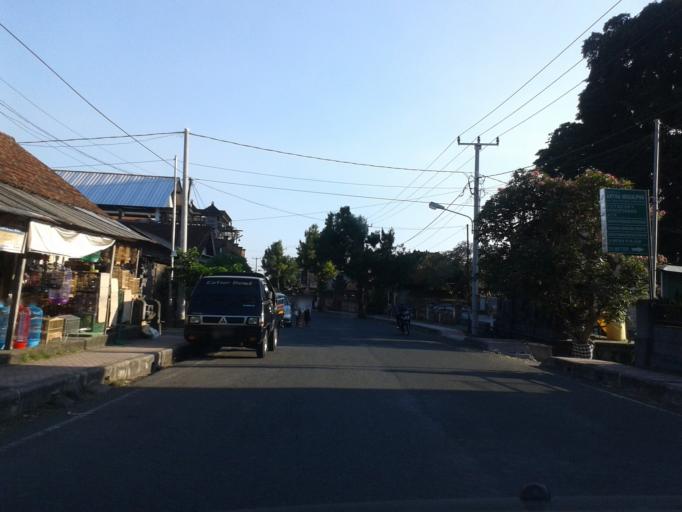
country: ID
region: Bali
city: Klungkung
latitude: -8.5170
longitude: 115.4010
